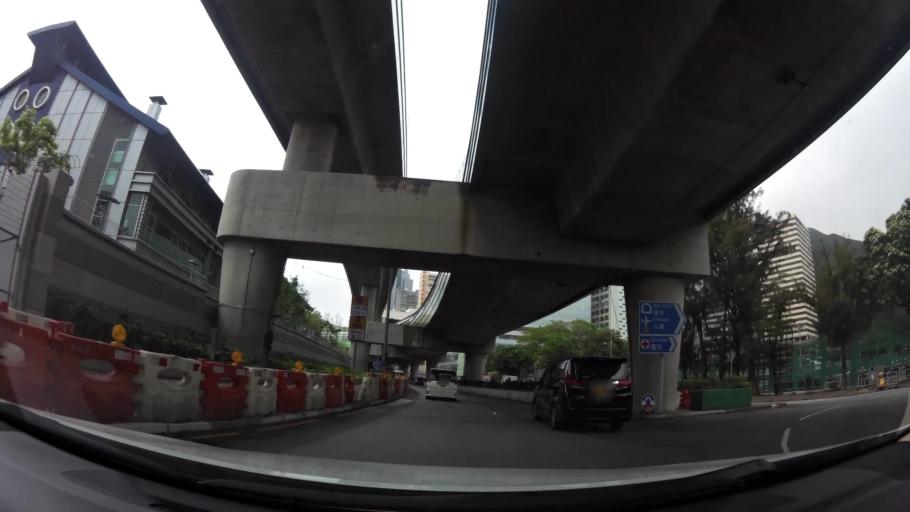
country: HK
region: Wanchai
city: Wan Chai
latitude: 22.2484
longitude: 114.1711
